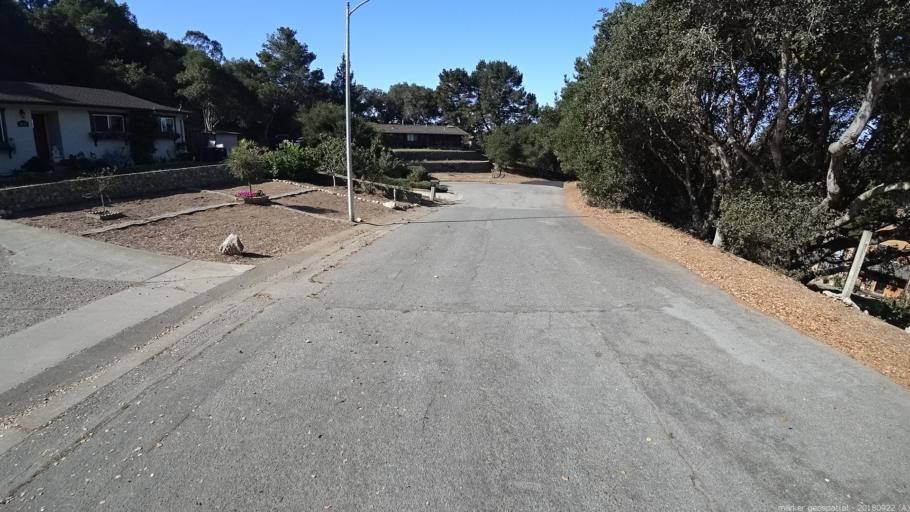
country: US
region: California
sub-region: Monterey County
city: Prunedale
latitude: 36.8059
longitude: -121.6621
